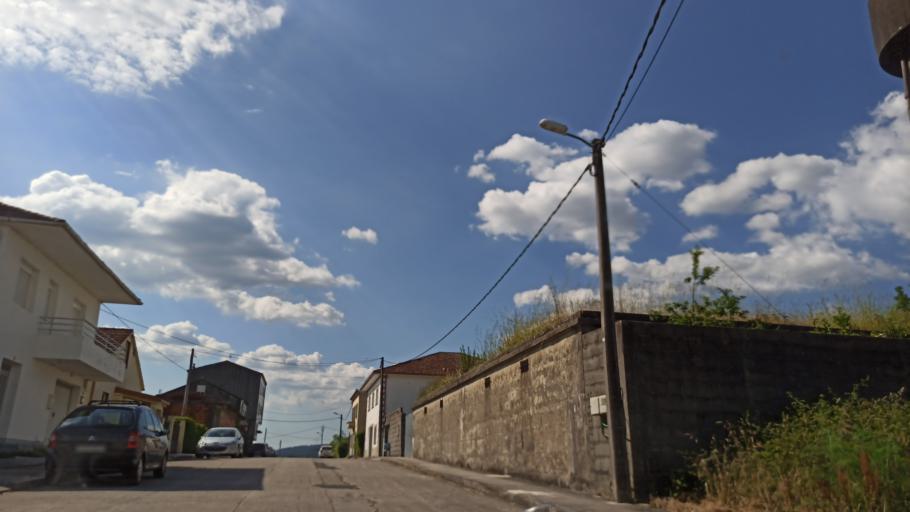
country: ES
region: Galicia
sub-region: Provincia da Coruna
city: Negreira
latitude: 42.9116
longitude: -8.7411
